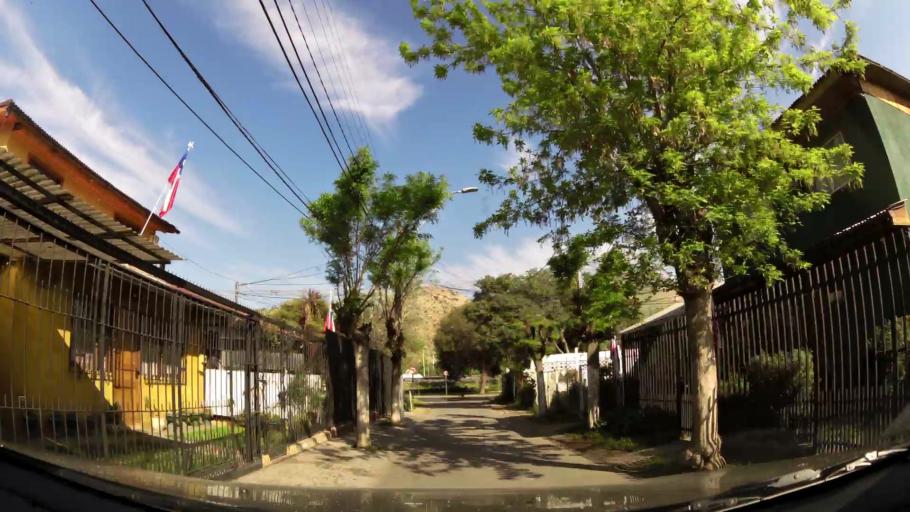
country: CL
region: Santiago Metropolitan
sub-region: Provincia de Maipo
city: San Bernardo
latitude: -33.6026
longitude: -70.7156
